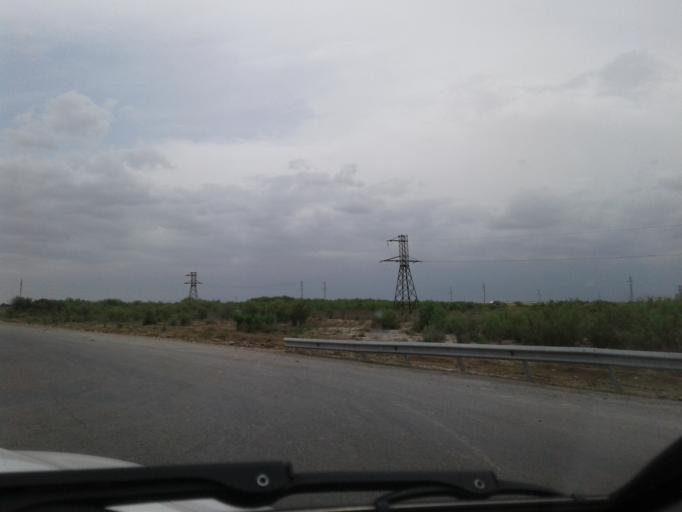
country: TM
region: Ahal
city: Kaka
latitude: 37.4850
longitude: 59.4749
